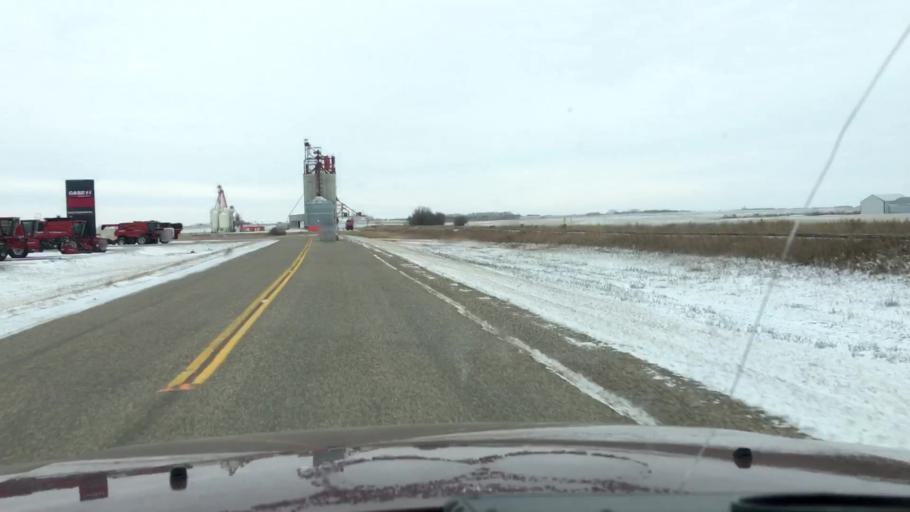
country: CA
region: Saskatchewan
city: Watrous
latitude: 51.2509
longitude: -105.9785
